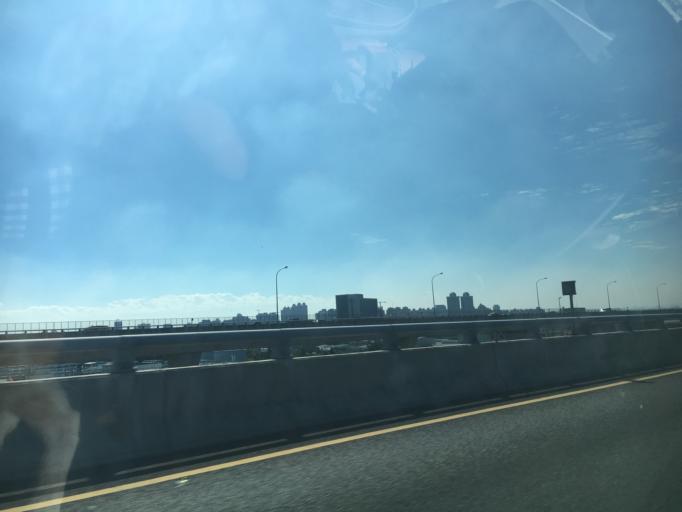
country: TW
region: Taiwan
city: Taoyuan City
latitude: 25.0411
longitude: 121.3026
